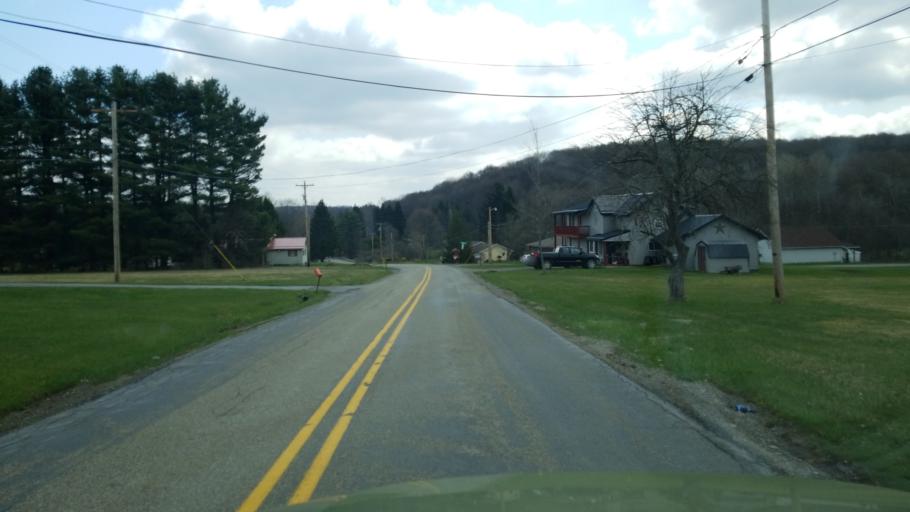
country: US
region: Pennsylvania
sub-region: Jefferson County
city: Brockway
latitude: 41.2729
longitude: -78.8307
